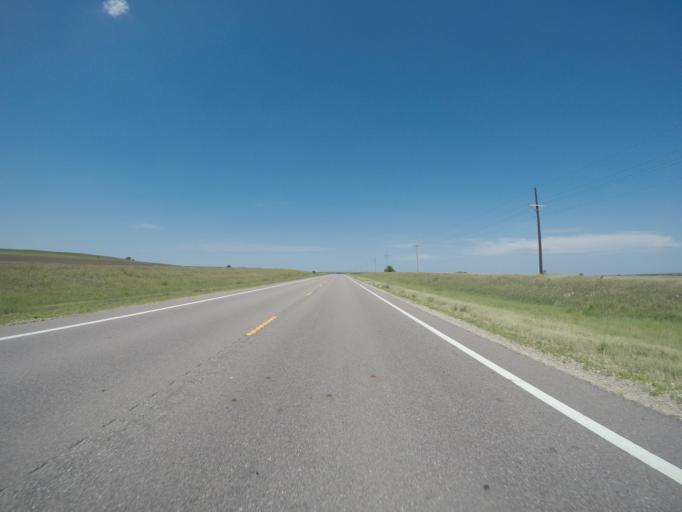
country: US
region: Kansas
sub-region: Osborne County
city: Osborne
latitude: 39.5101
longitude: -98.6787
